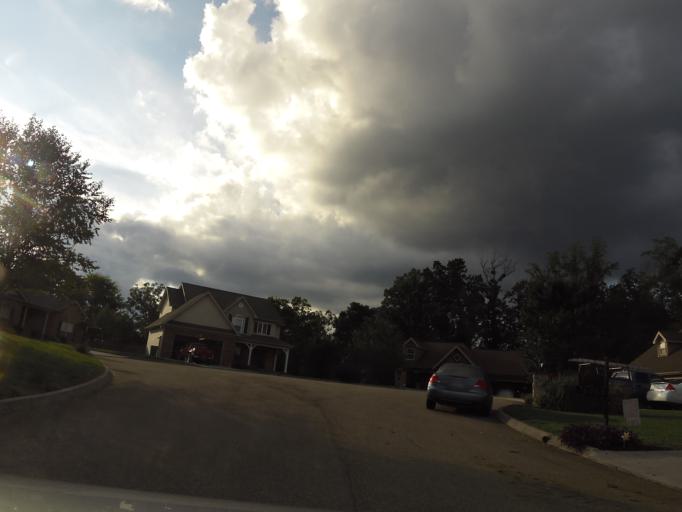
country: US
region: Tennessee
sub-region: Knox County
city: Knoxville
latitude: 36.0029
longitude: -84.0159
